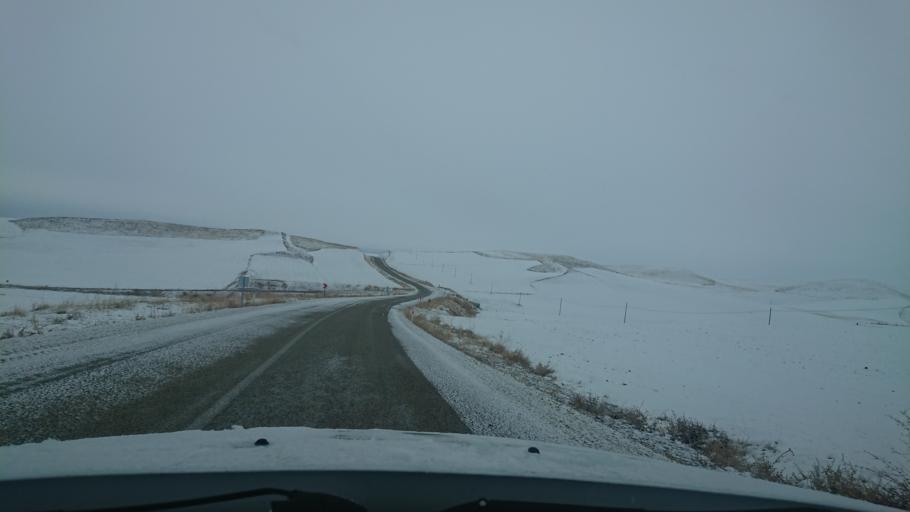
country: TR
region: Aksaray
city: Agacoren
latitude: 38.7859
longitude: 33.8710
